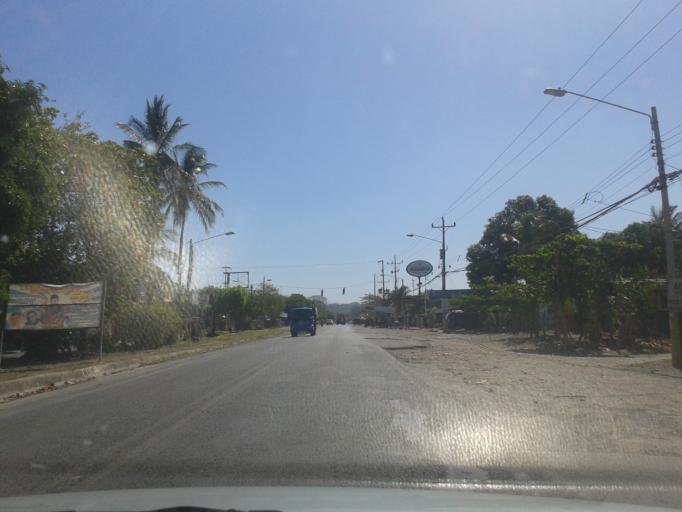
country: CR
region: Puntarenas
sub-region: Canton Central de Puntarenas
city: Chacarita
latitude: 9.9780
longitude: -84.7367
